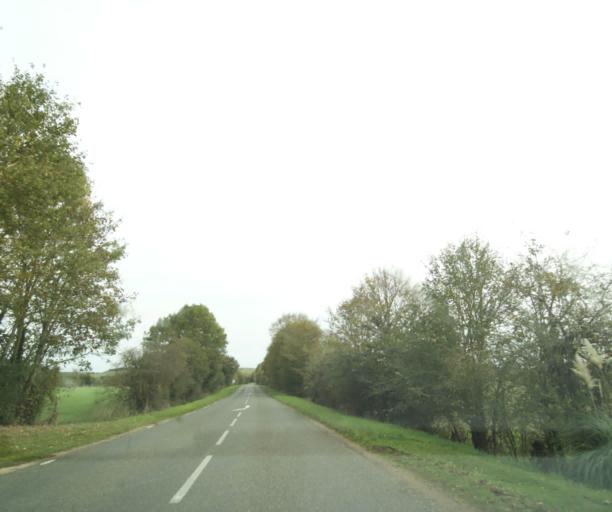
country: FR
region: Centre
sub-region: Departement d'Eure-et-Loir
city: Cherisy
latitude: 48.7547
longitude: 1.4003
